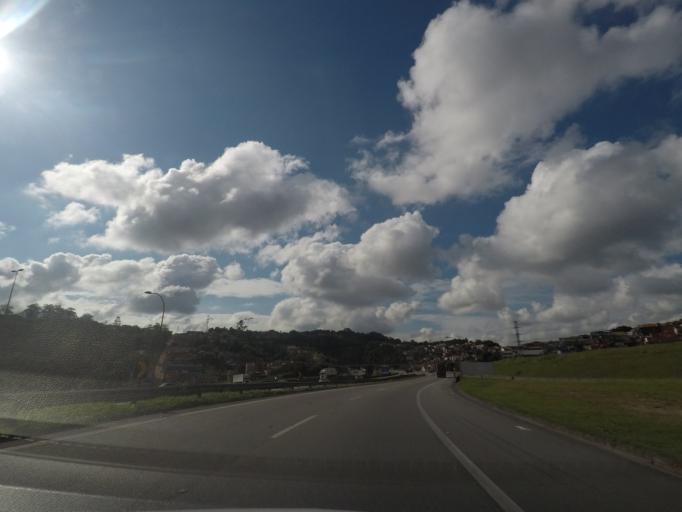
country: BR
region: Sao Paulo
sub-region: Embu
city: Embu
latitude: -23.6313
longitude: -46.8306
